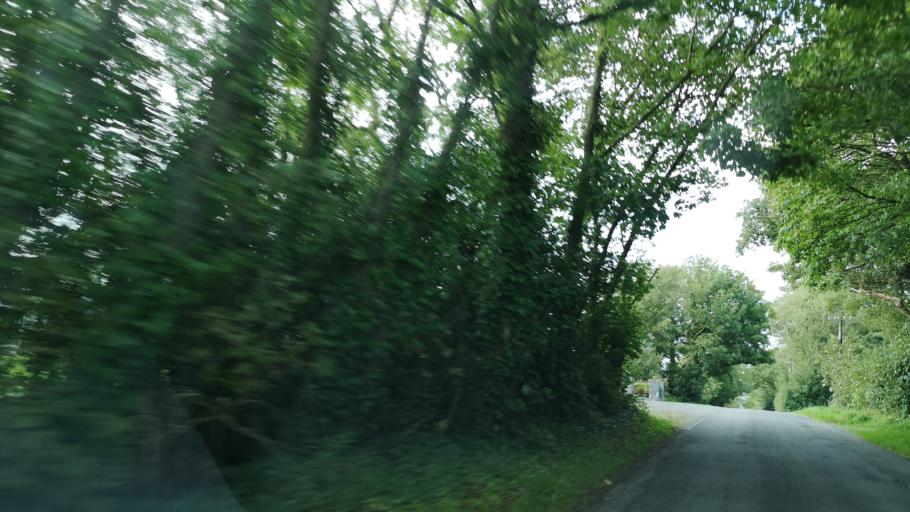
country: IE
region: Connaught
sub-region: County Galway
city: Ballinasloe
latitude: 53.3199
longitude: -8.1037
